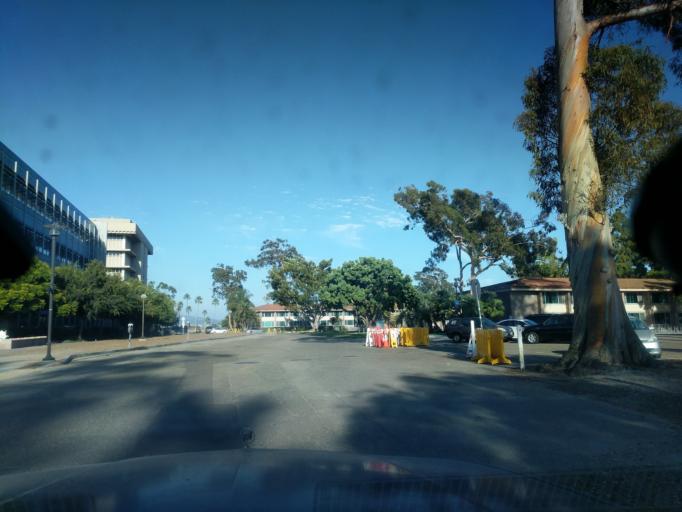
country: US
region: California
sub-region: Santa Barbara County
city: Isla Vista
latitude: 34.4116
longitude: -119.8445
